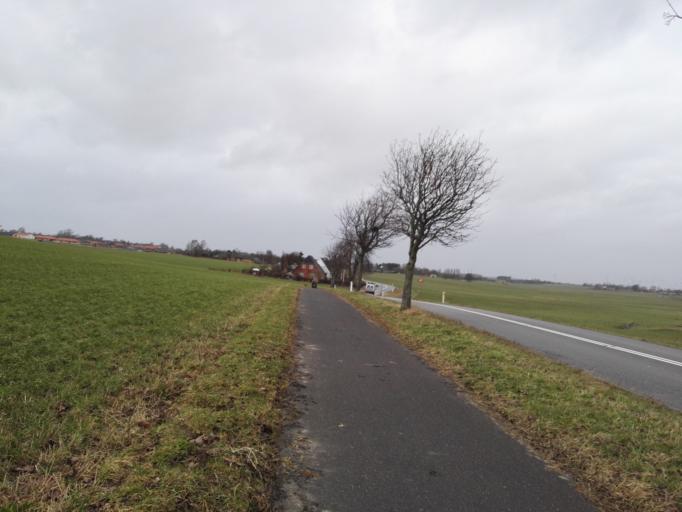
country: DK
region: Zealand
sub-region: Lejre Kommune
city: Ejby
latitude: 55.6952
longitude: 11.9092
